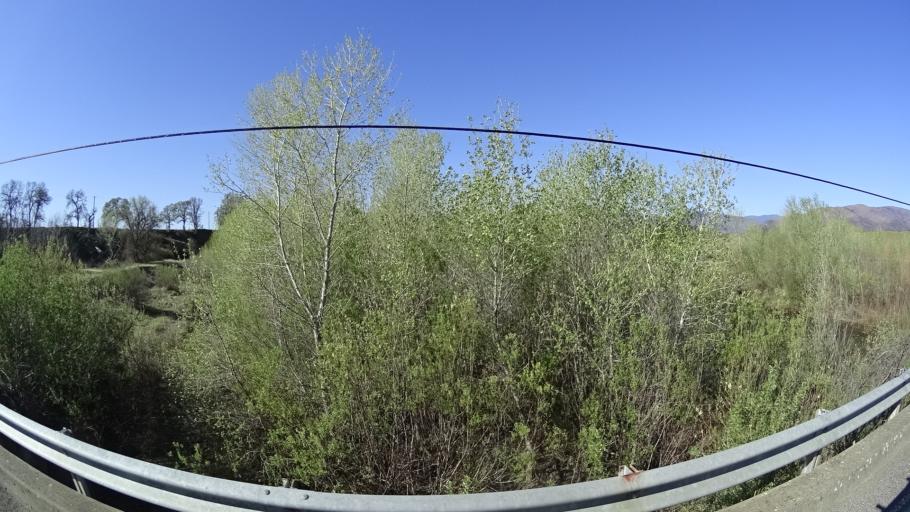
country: US
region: California
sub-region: Glenn County
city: Orland
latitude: 39.6790
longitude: -122.5305
